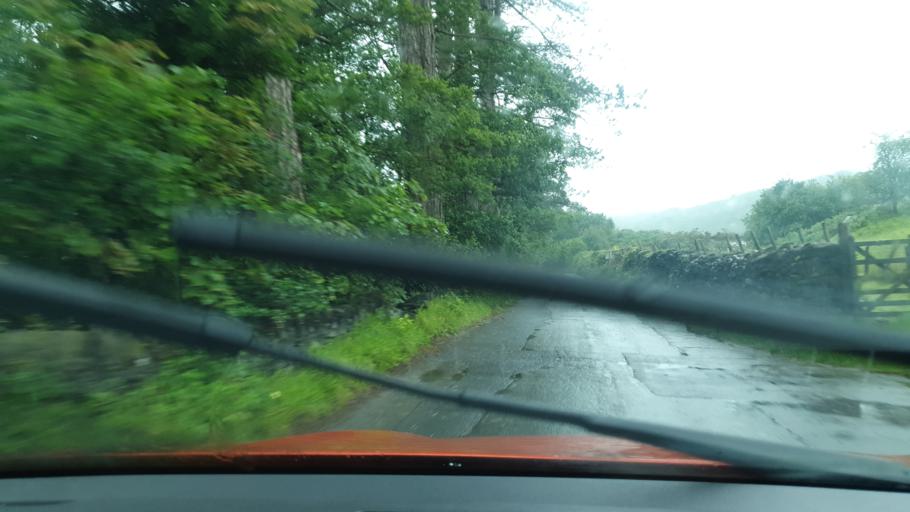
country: GB
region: England
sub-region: Cumbria
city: Millom
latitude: 54.3277
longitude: -3.2357
